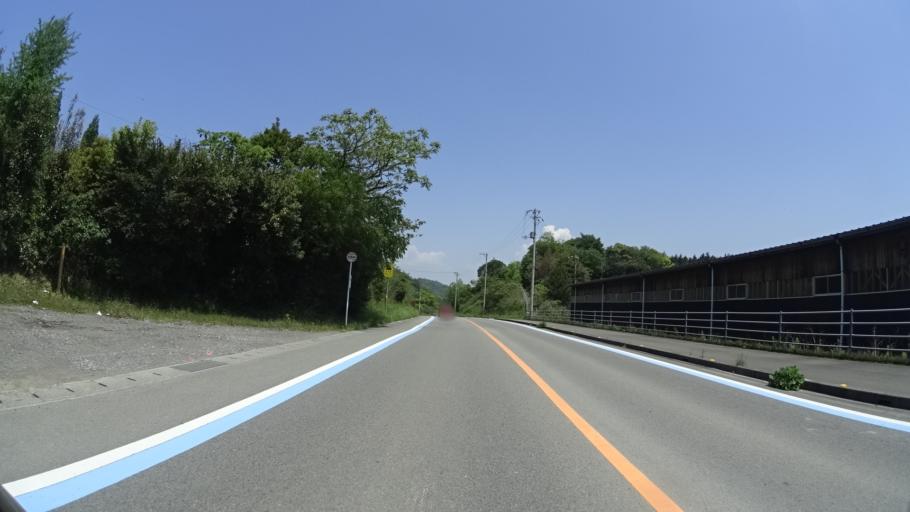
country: JP
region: Ehime
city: Iyo
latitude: 33.7190
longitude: 132.6771
